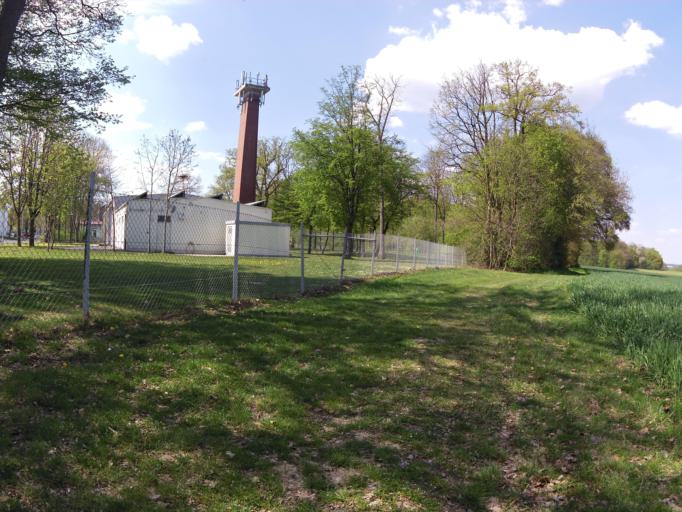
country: DE
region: Bavaria
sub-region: Regierungsbezirk Unterfranken
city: Giebelstadt
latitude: 49.6891
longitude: 9.9526
